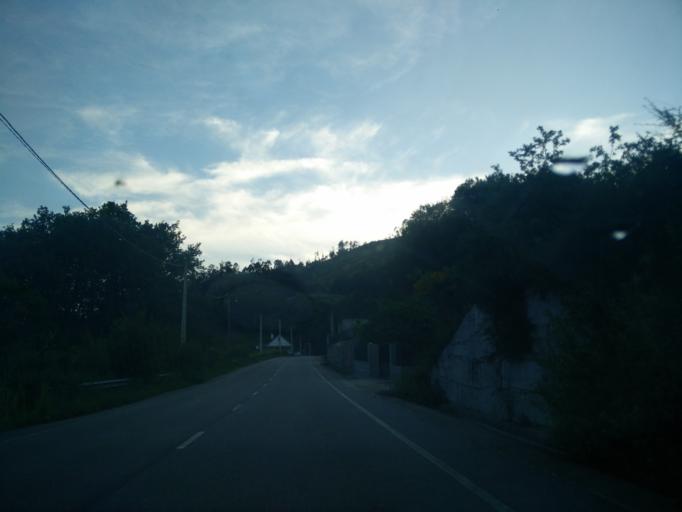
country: ES
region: Galicia
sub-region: Provincia de Pontevedra
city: Mondariz
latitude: 42.2430
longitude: -8.4488
